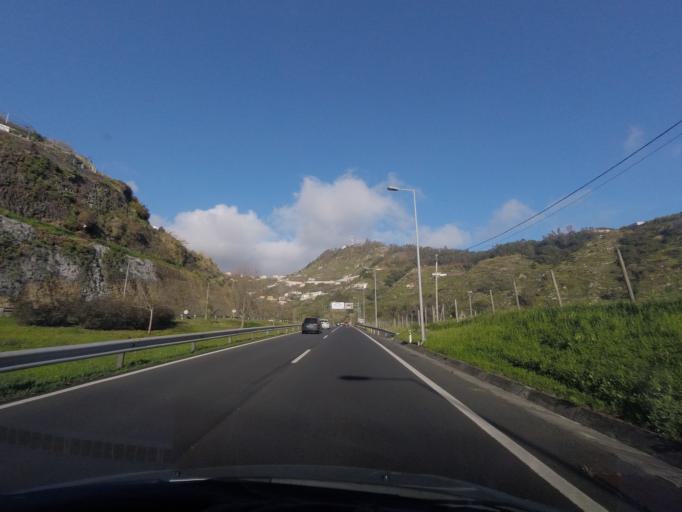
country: PT
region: Madeira
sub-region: Ribeira Brava
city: Campanario
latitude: 32.6583
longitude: -17.0162
